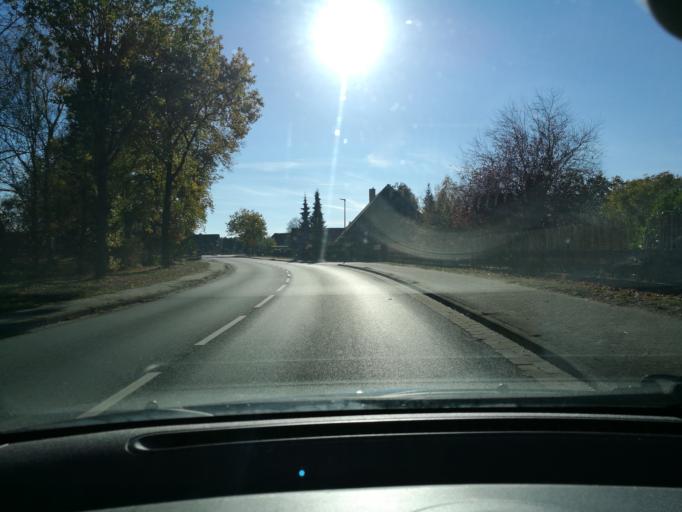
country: DE
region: Lower Saxony
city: Dannenberg
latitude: 53.0873
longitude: 11.0699
